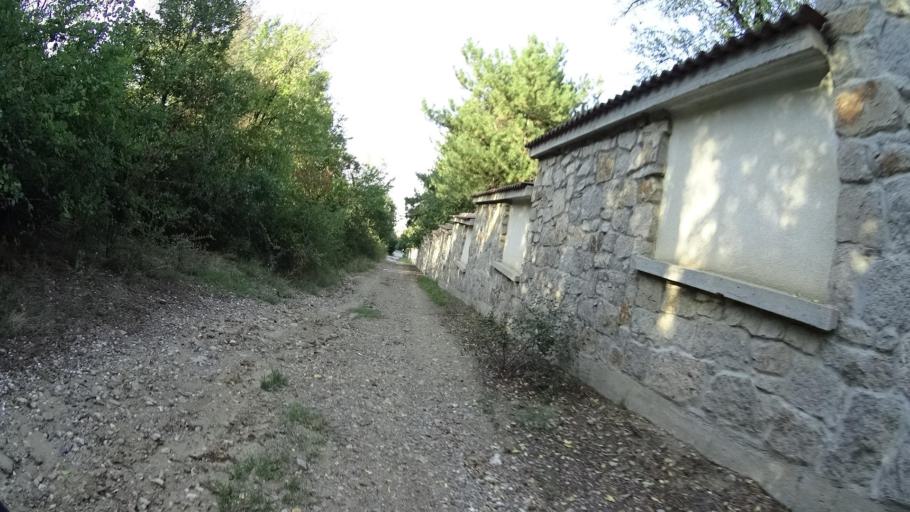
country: BG
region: Plovdiv
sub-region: Obshtina Plovdiv
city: Plovdiv
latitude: 42.0597
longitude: 24.6982
